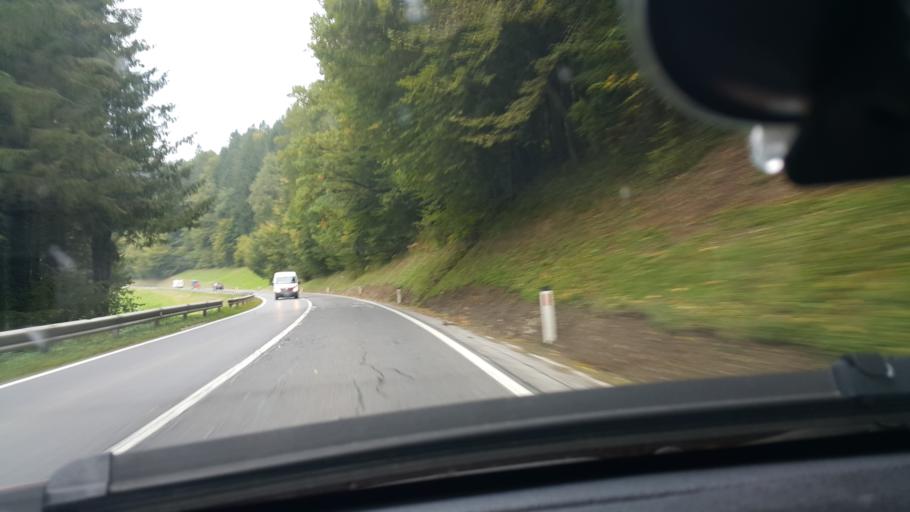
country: SI
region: Radlje ob Dravi
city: Radlje ob Dravi
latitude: 46.5951
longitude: 15.2686
